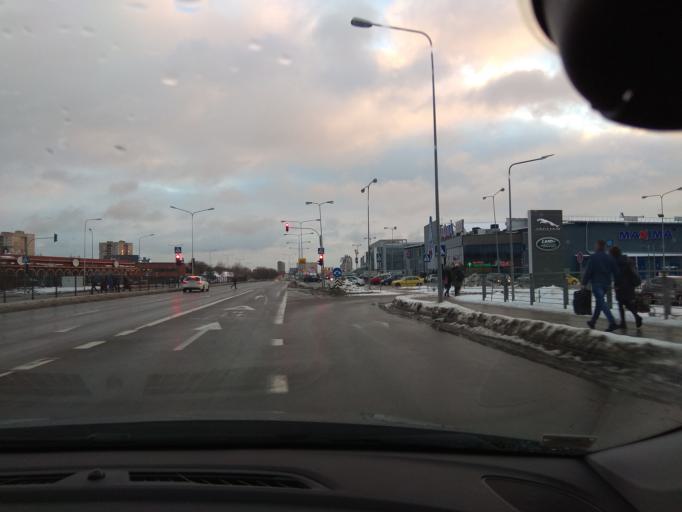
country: LT
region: Vilnius County
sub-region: Vilnius
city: Fabijoniskes
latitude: 54.7291
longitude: 25.2392
